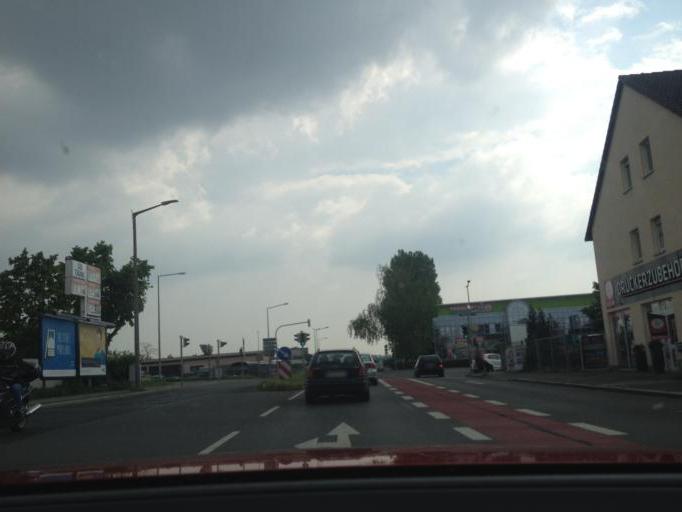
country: DE
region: Bavaria
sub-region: Regierungsbezirk Mittelfranken
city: Grossreuth bei Schweinau
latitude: 49.4418
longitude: 11.0155
